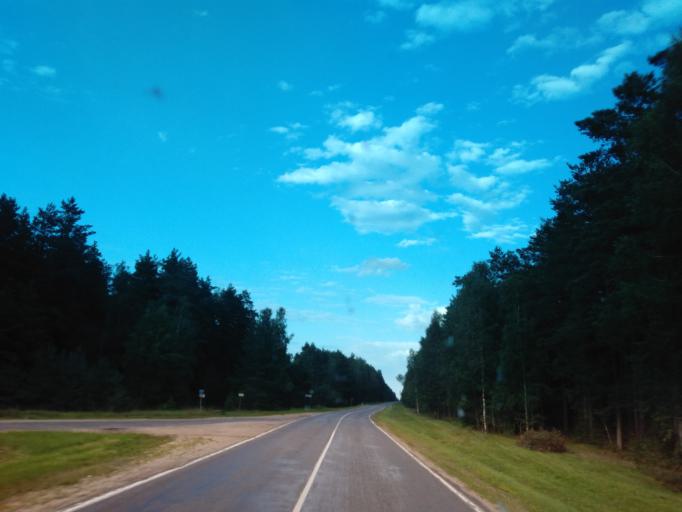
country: BY
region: Minsk
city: Uzda
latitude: 53.4198
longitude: 27.4202
